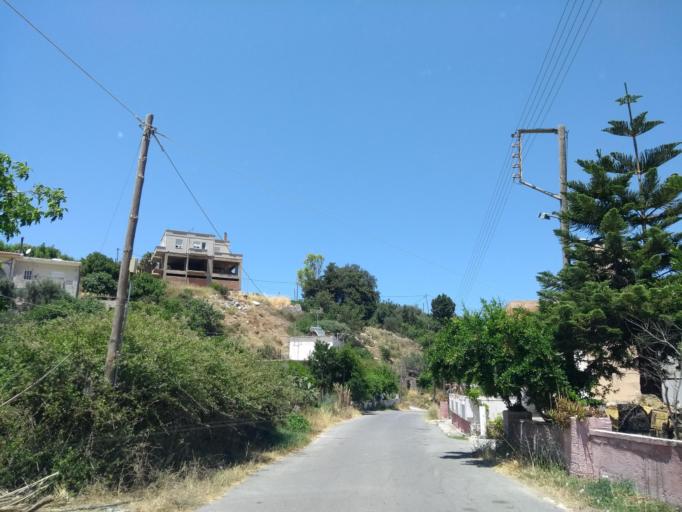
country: GR
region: Crete
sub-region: Nomos Chanias
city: Georgioupolis
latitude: 35.3157
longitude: 24.3014
